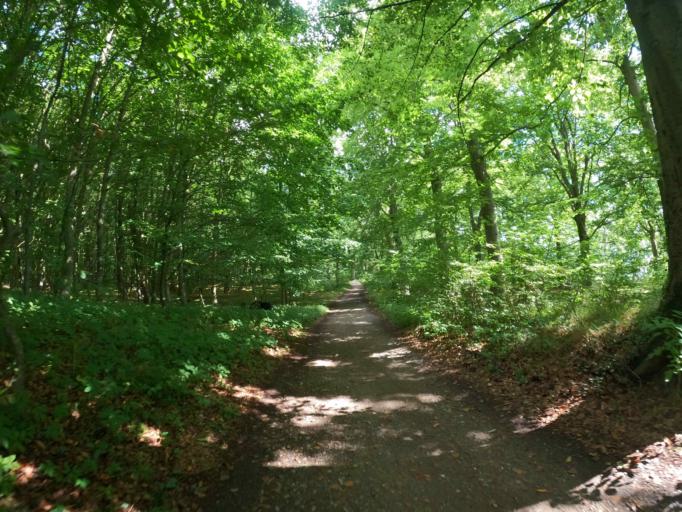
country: DE
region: Mecklenburg-Vorpommern
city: Putbus
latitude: 54.3417
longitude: 13.5163
